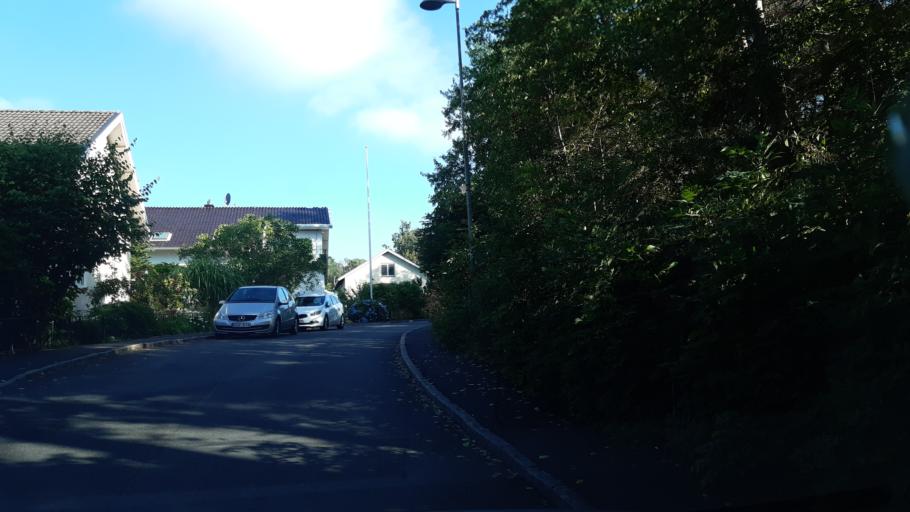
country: SE
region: Vaestra Goetaland
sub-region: Goteborg
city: Eriksbo
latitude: 57.7190
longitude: 12.0412
